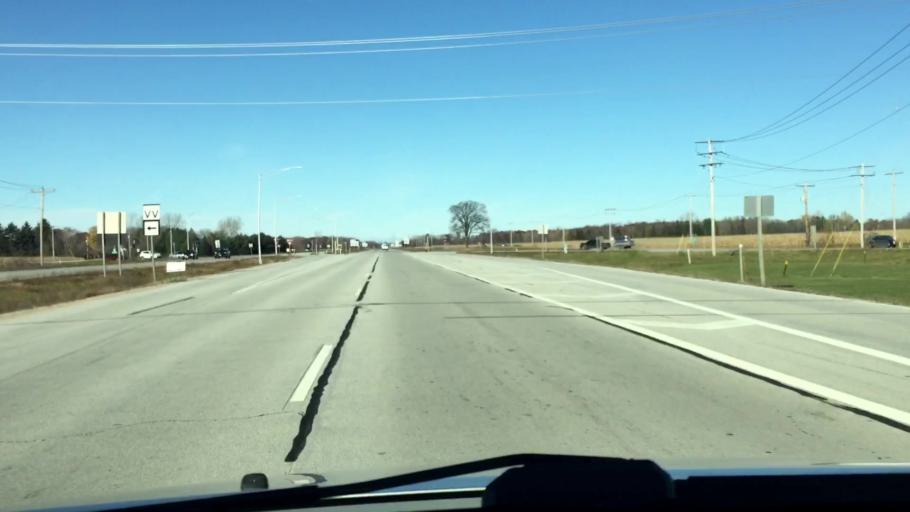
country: US
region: Wisconsin
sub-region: Brown County
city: Oneida
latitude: 44.5740
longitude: -88.1642
